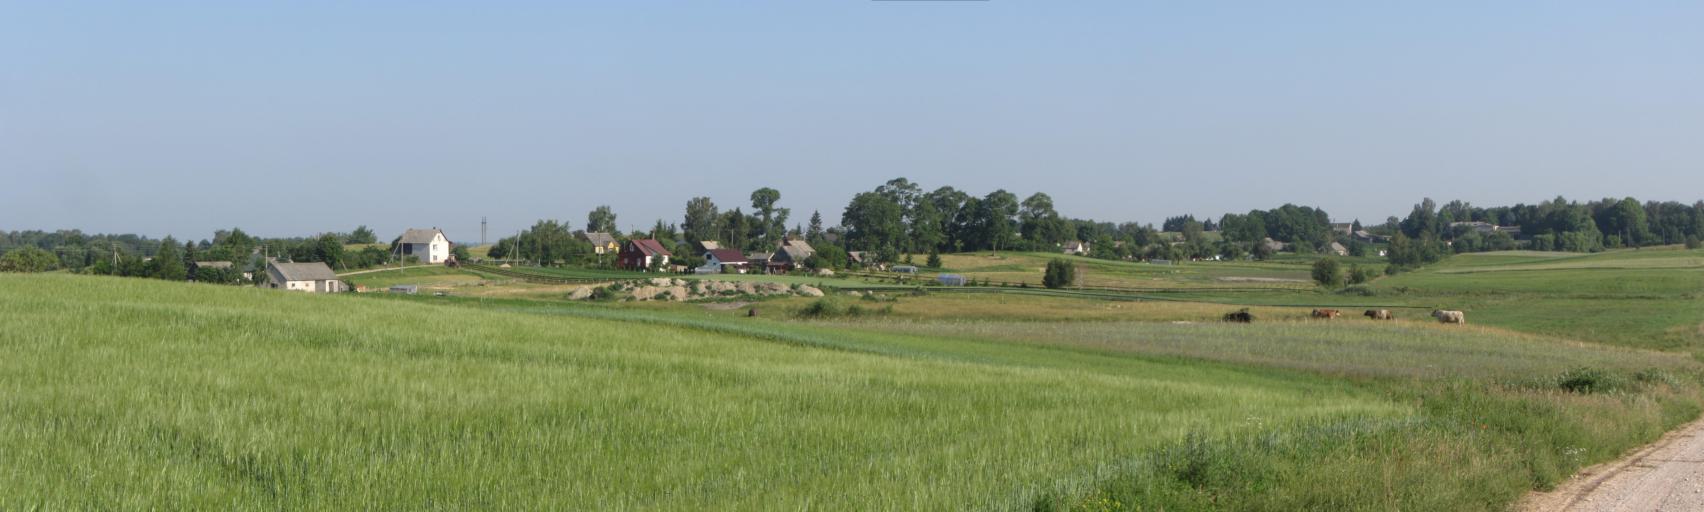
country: LT
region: Alytaus apskritis
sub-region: Alytus
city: Alytus
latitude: 54.2641
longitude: 23.8930
